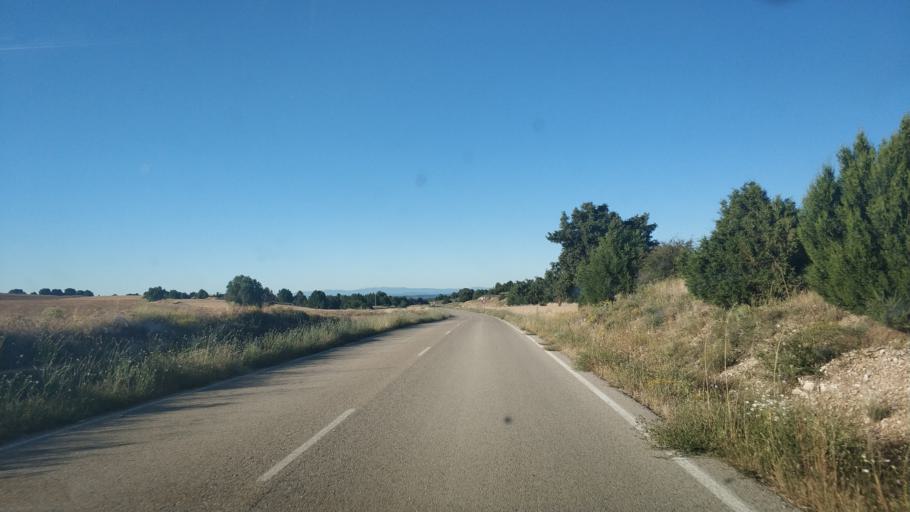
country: ES
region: Castille and Leon
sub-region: Provincia de Soria
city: San Esteban de Gormaz
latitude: 41.4843
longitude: -3.2108
